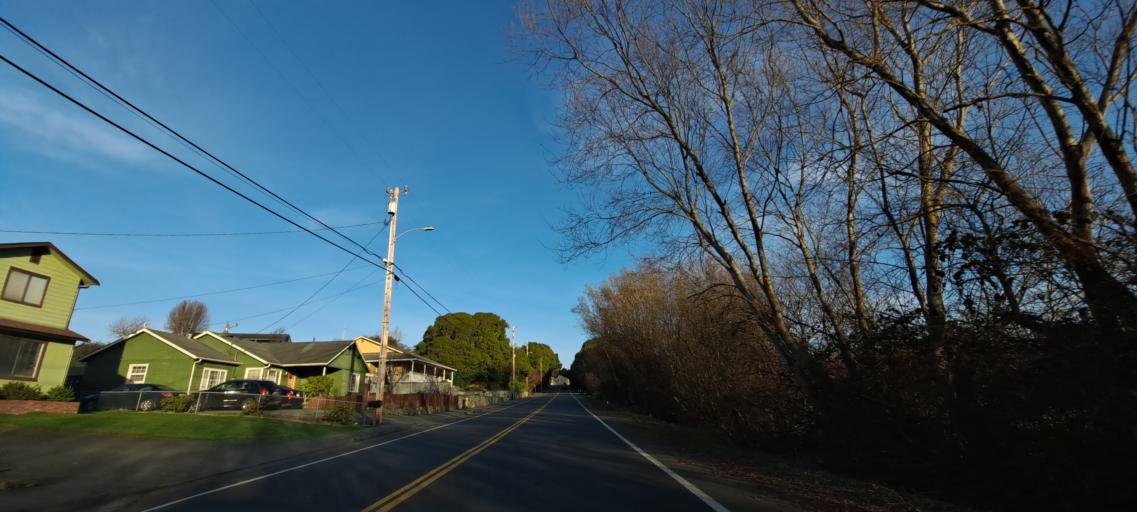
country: US
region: California
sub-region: Humboldt County
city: Fortuna
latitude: 40.5775
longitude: -124.1440
